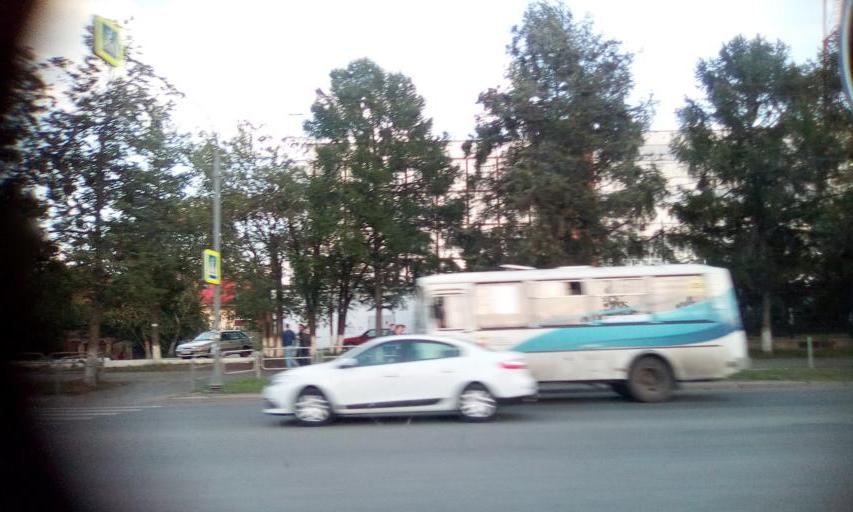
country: RU
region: Chelyabinsk
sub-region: Gorod Chelyabinsk
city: Chelyabinsk
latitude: 55.1431
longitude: 61.3778
